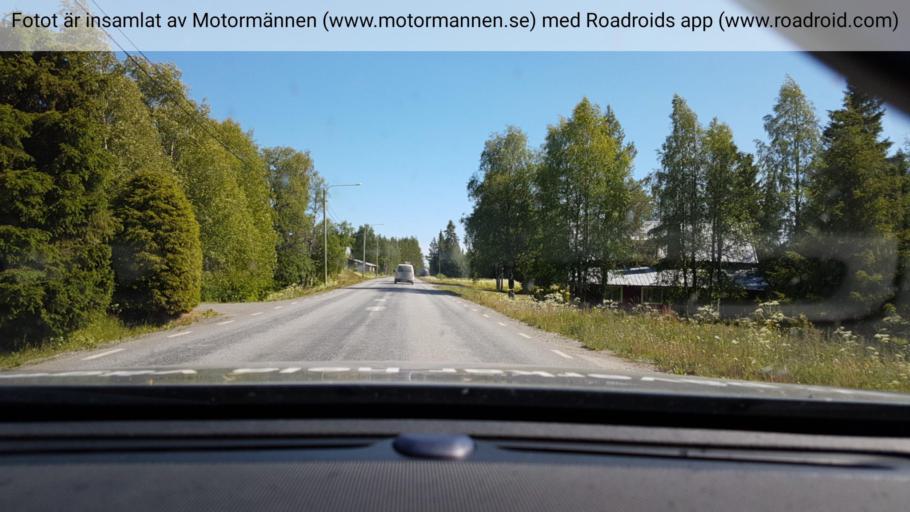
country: SE
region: Vaesterbotten
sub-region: Vilhelmina Kommun
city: Sjoberg
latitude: 64.6909
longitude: 16.2695
